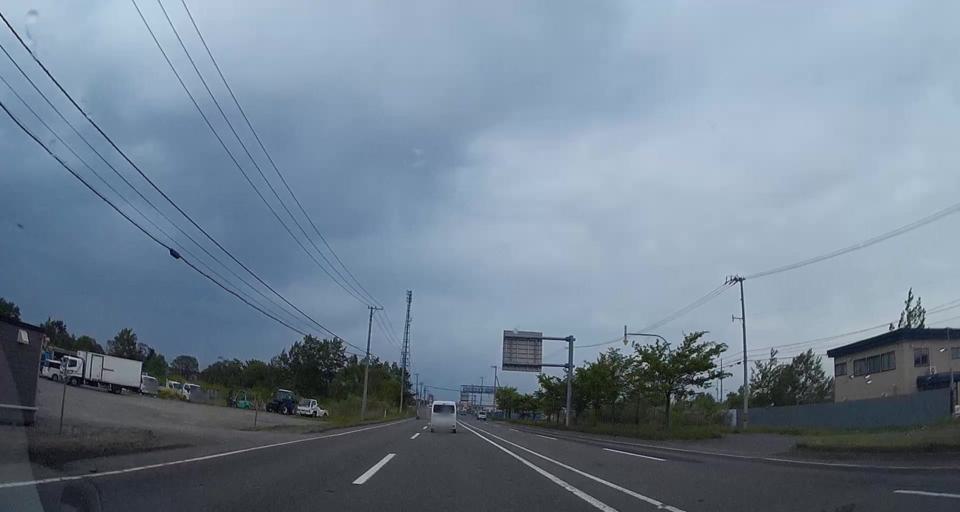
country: JP
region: Hokkaido
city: Tomakomai
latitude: 42.6756
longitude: 141.7090
